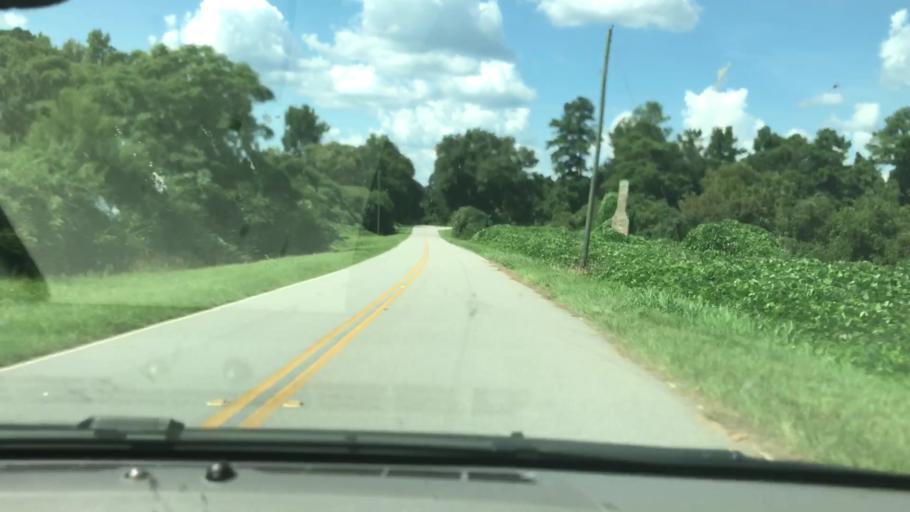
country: US
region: Georgia
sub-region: Troup County
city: La Grange
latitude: 33.0860
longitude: -85.1294
